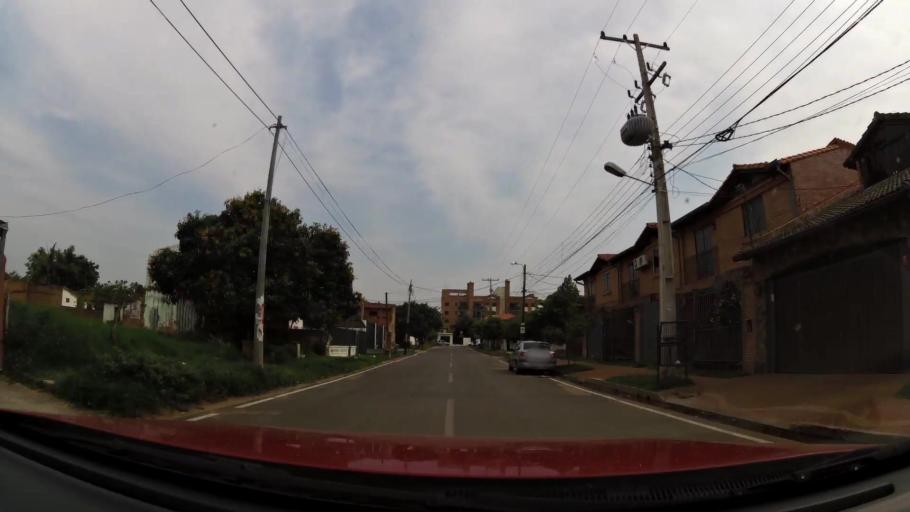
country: PY
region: Central
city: Fernando de la Mora
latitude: -25.2827
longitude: -57.5491
